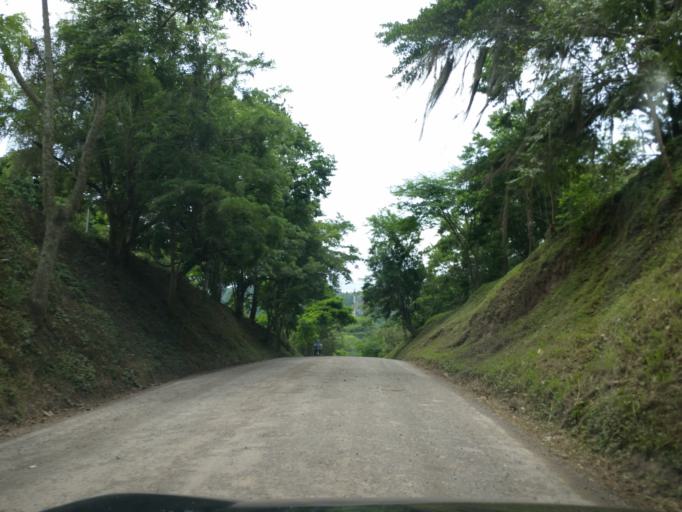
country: NI
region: Matagalpa
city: San Ramon
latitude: 12.9386
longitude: -85.8685
